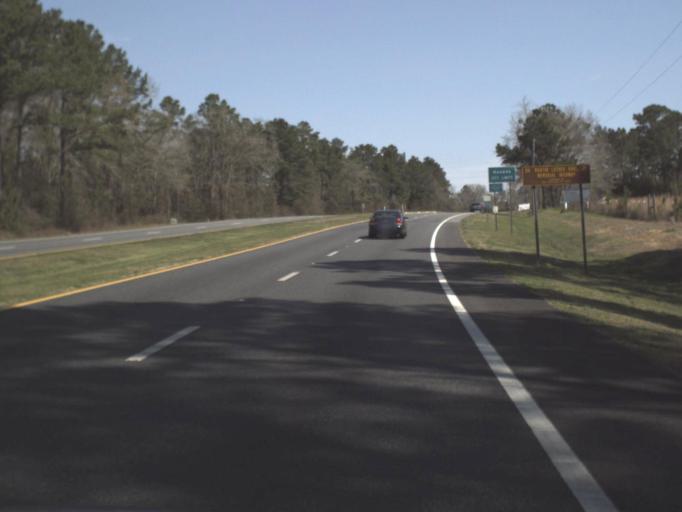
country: US
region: Florida
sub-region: Gadsden County
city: Havana
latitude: 30.6116
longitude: -84.4232
